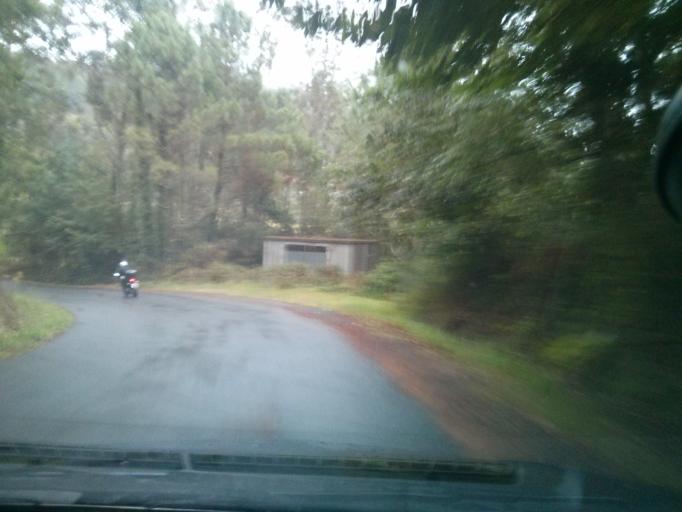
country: ES
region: Galicia
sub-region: Provincia da Coruna
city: Outes
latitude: 42.8396
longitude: -8.8642
